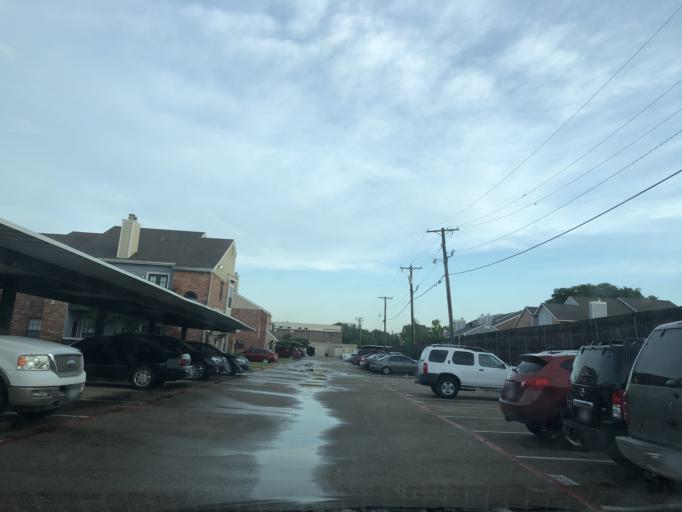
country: US
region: Texas
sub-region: Dallas County
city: Garland
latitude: 32.8414
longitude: -96.6214
